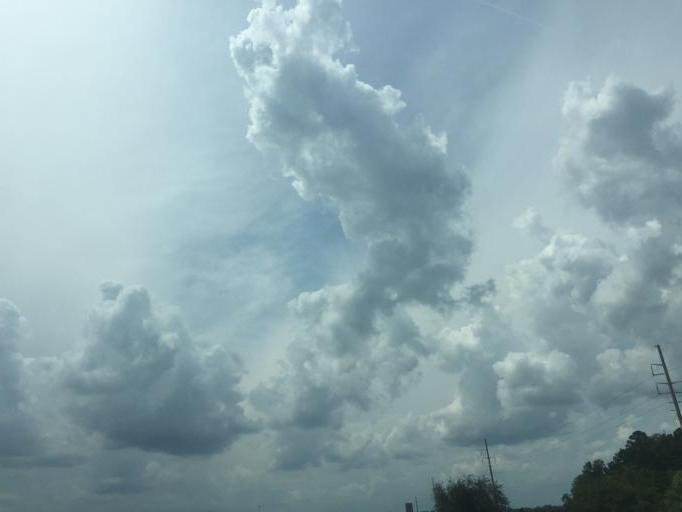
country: US
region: Georgia
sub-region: Chatham County
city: Skidaway Island
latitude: 31.9501
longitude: -81.0802
